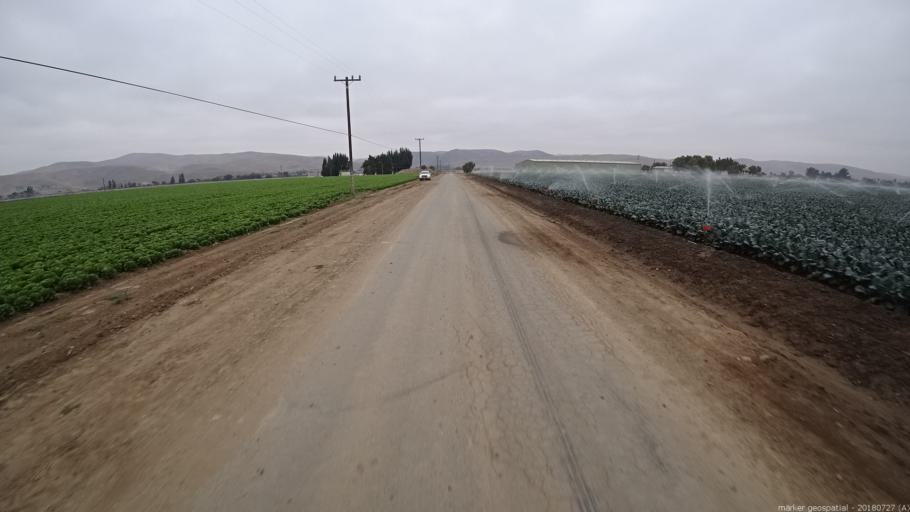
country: US
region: California
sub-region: Monterey County
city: Greenfield
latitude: 36.3390
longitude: -121.2266
